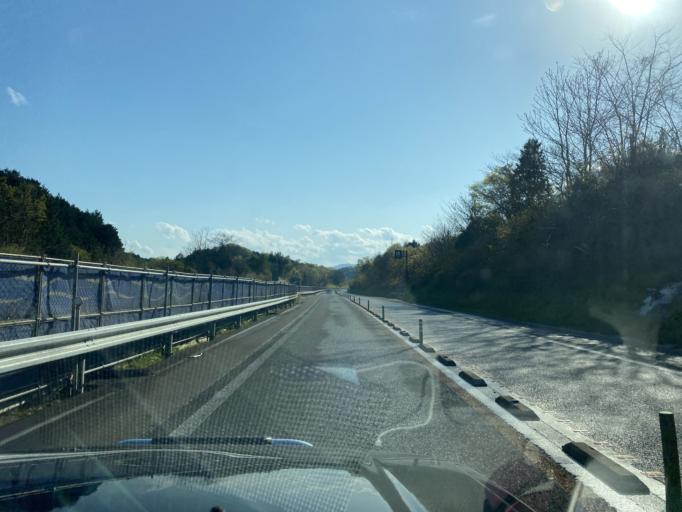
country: JP
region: Kyoto
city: Ayabe
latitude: 35.3267
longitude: 135.2231
